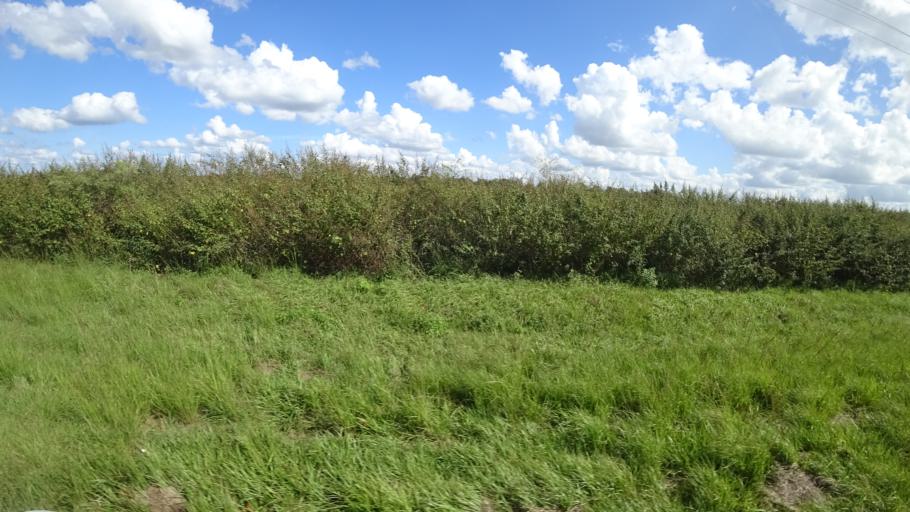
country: US
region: Florida
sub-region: Sarasota County
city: Lake Sarasota
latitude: 27.3725
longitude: -82.1409
